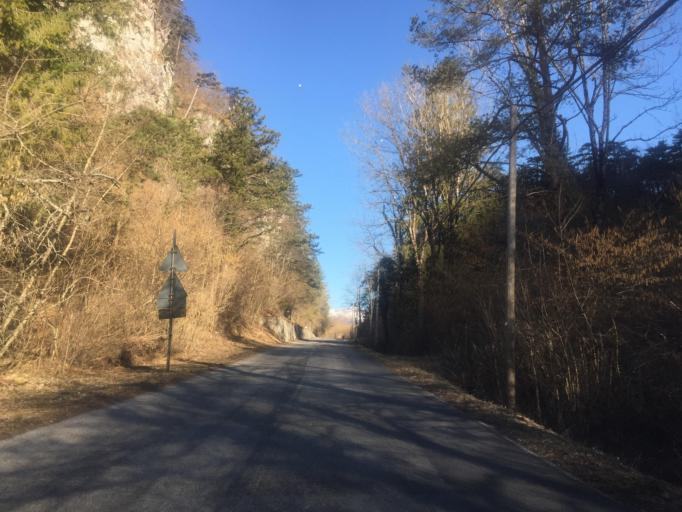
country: IT
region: Friuli Venezia Giulia
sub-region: Provincia di Udine
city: Tolmezzo
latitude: 46.4173
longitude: 13.0504
